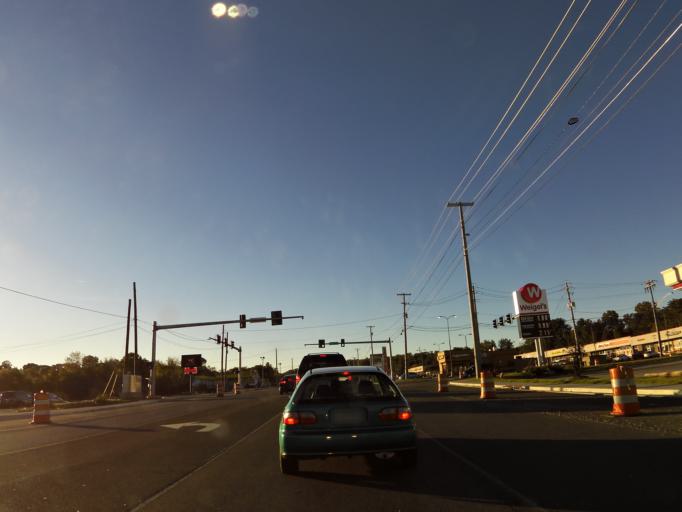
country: US
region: Tennessee
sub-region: Knox County
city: Knoxville
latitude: 35.9785
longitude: -84.0133
